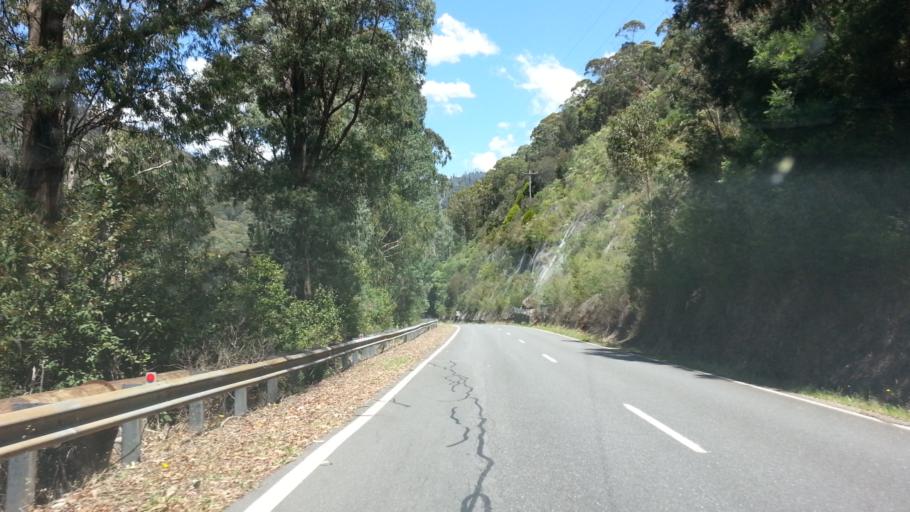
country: AU
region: Victoria
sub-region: Alpine
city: Mount Beauty
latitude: -36.7808
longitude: 147.2179
